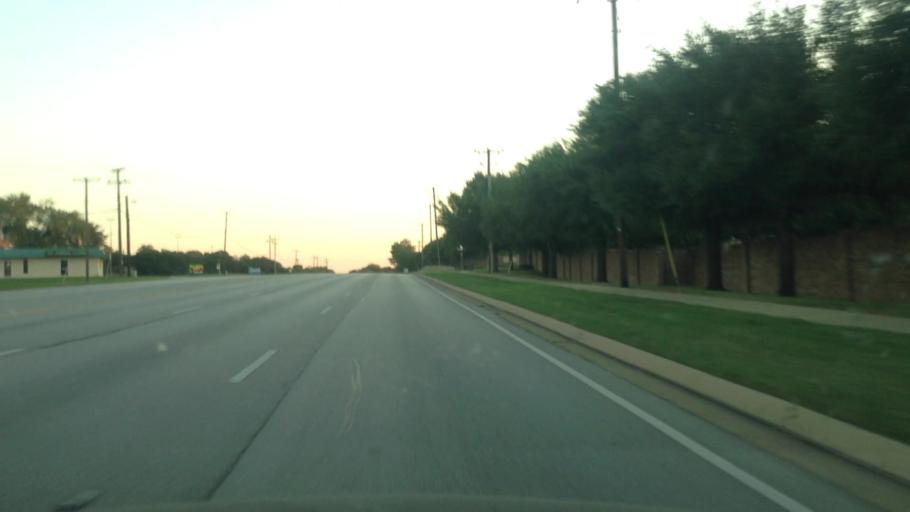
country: US
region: Texas
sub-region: Tarrant County
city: North Richland Hills
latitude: 32.8540
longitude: -97.2128
